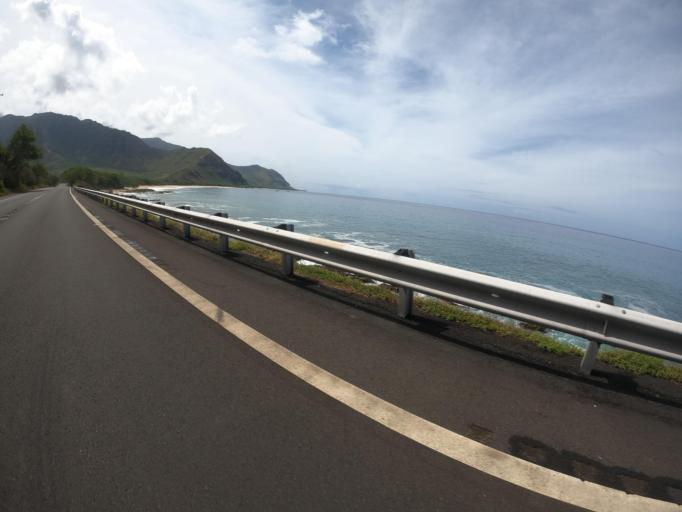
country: US
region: Hawaii
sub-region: Honolulu County
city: Makaha Valley
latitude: 21.5388
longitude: -158.2338
